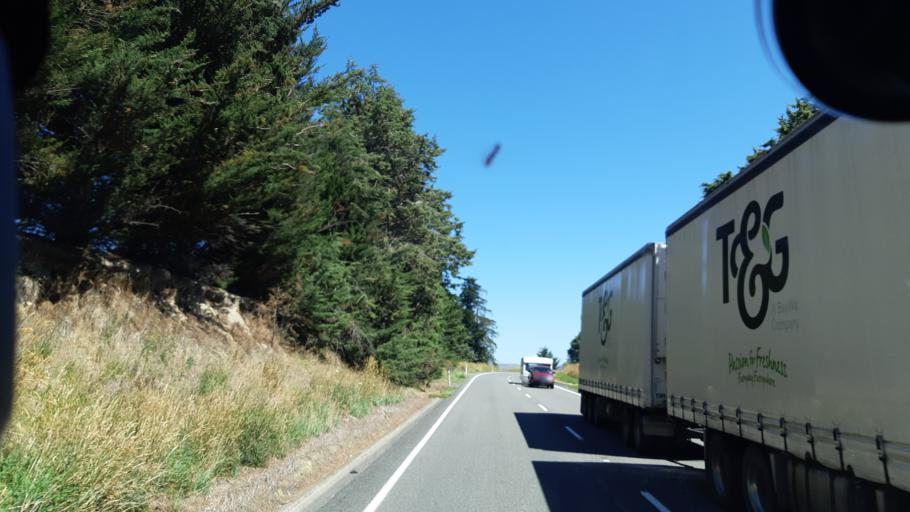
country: NZ
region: Canterbury
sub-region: Kaikoura District
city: Kaikoura
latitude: -42.7508
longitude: 173.2707
